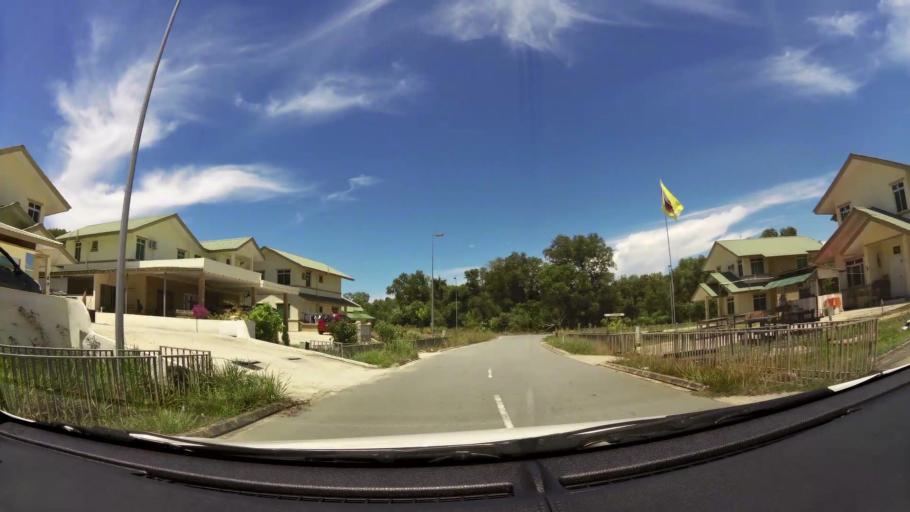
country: BN
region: Brunei and Muara
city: Bandar Seri Begawan
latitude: 5.0284
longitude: 115.0348
